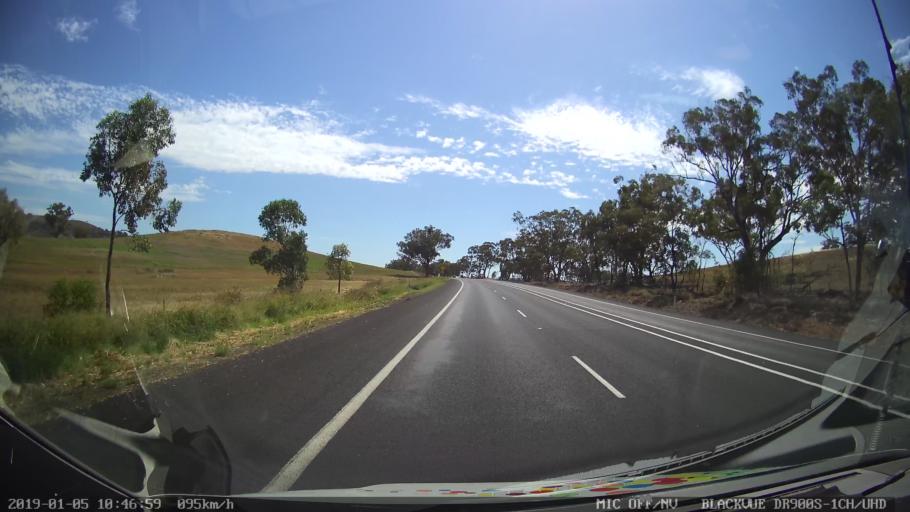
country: AU
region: New South Wales
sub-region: Warrumbungle Shire
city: Coonabarabran
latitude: -31.4483
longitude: 149.0268
